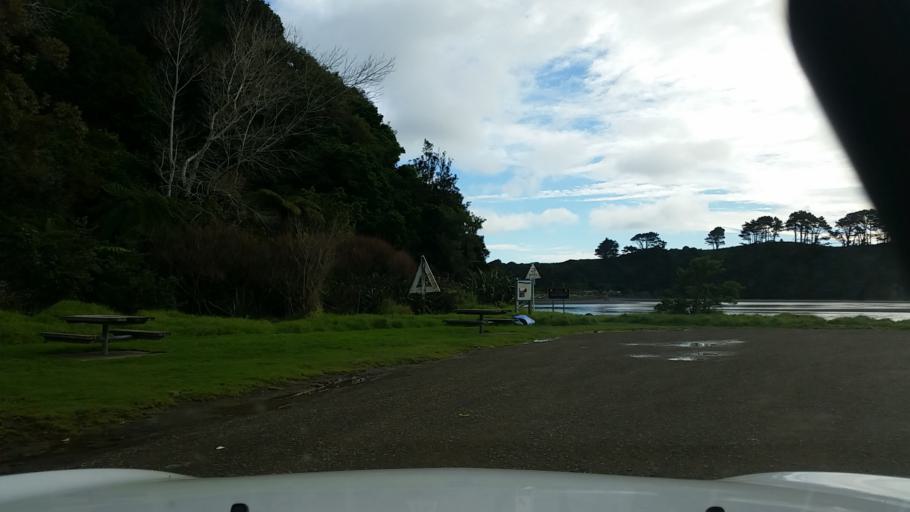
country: NZ
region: Taranaki
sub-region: New Plymouth District
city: Waitara
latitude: -38.8175
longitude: 174.5914
